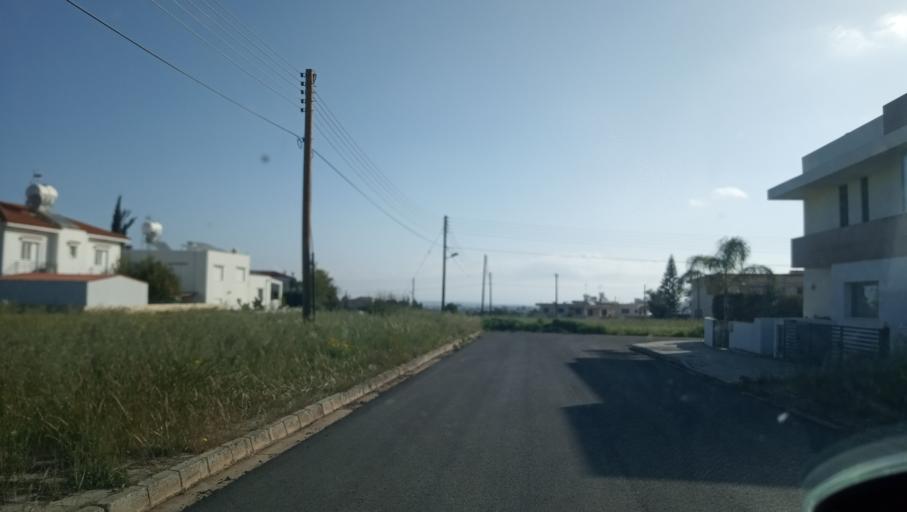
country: CY
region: Lefkosia
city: Tseri
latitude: 35.0801
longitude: 33.3183
